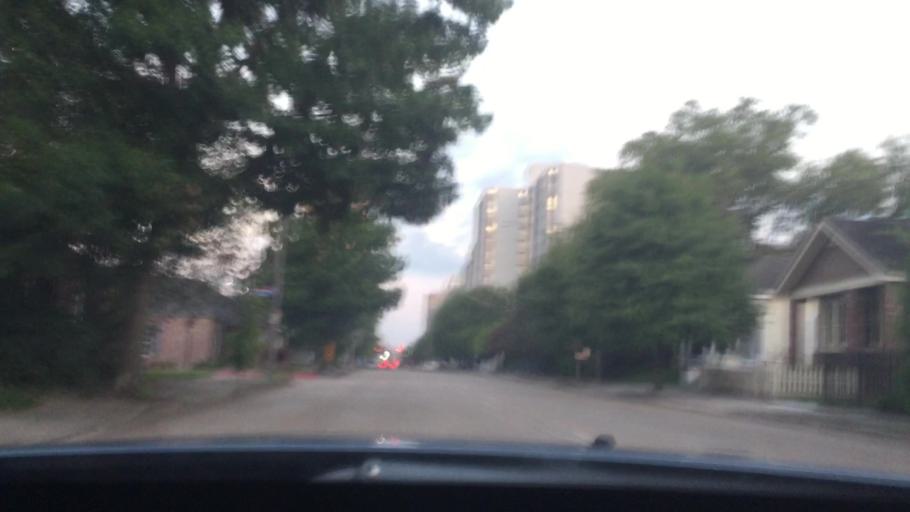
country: US
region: Louisiana
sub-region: East Baton Rouge Parish
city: Baton Rouge
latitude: 30.4527
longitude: -91.1820
